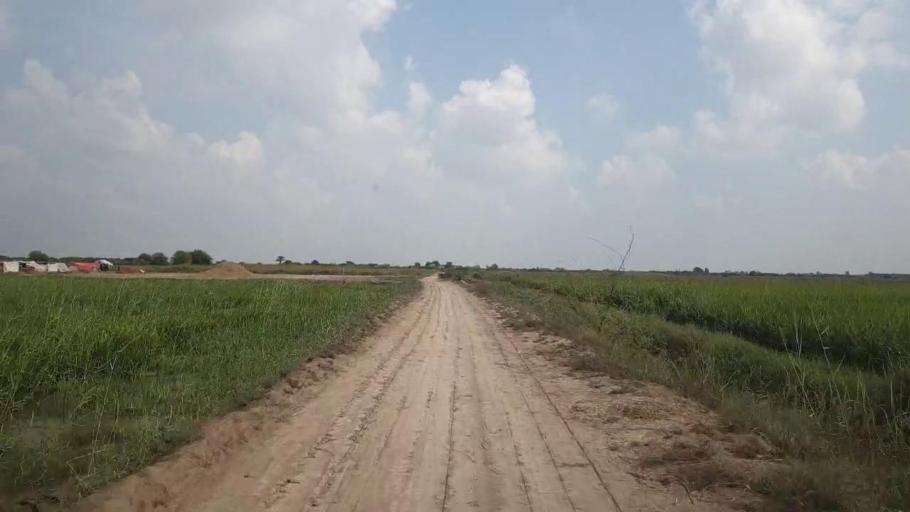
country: PK
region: Sindh
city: Badin
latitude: 24.5328
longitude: 68.6370
